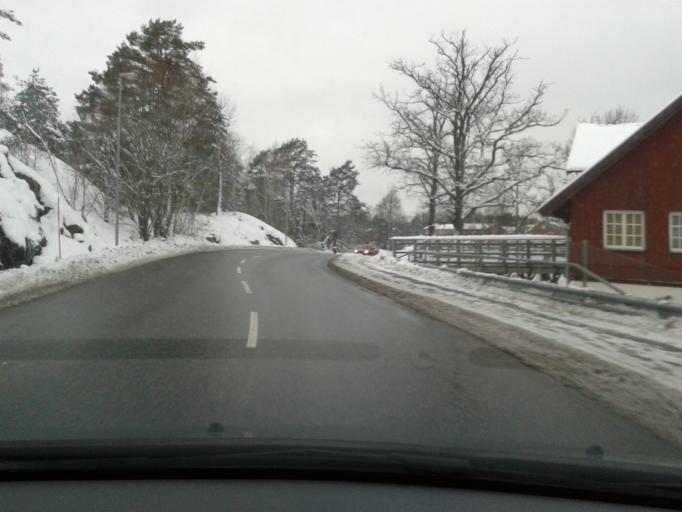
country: SE
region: Stockholm
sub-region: Nacka Kommun
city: Saltsjobaden
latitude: 59.2388
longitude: 18.2962
